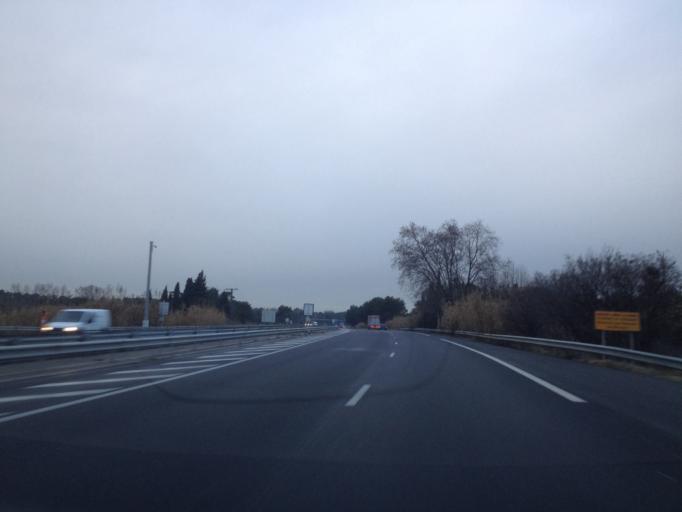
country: FR
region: Provence-Alpes-Cote d'Azur
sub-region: Departement des Bouches-du-Rhone
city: Aix-en-Provence
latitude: 43.5196
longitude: 5.4258
